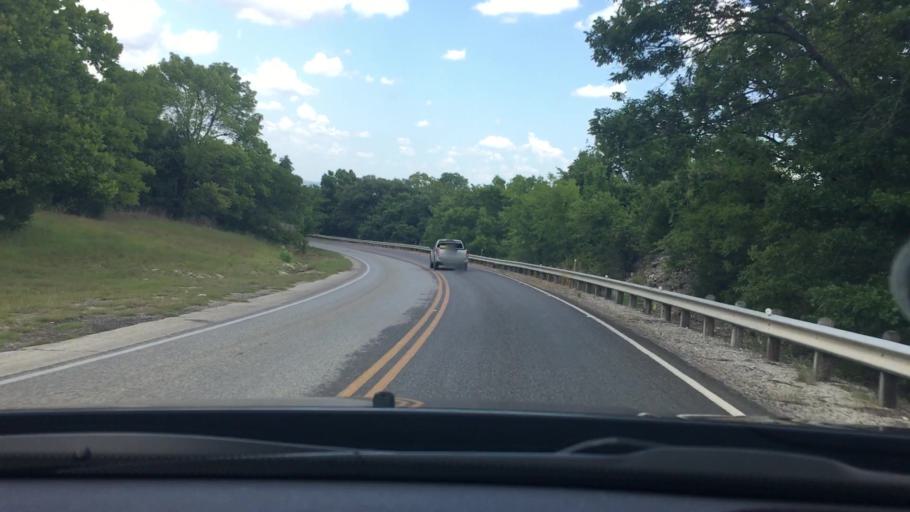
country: US
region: Oklahoma
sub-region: Pontotoc County
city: Ada
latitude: 34.5706
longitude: -96.6291
